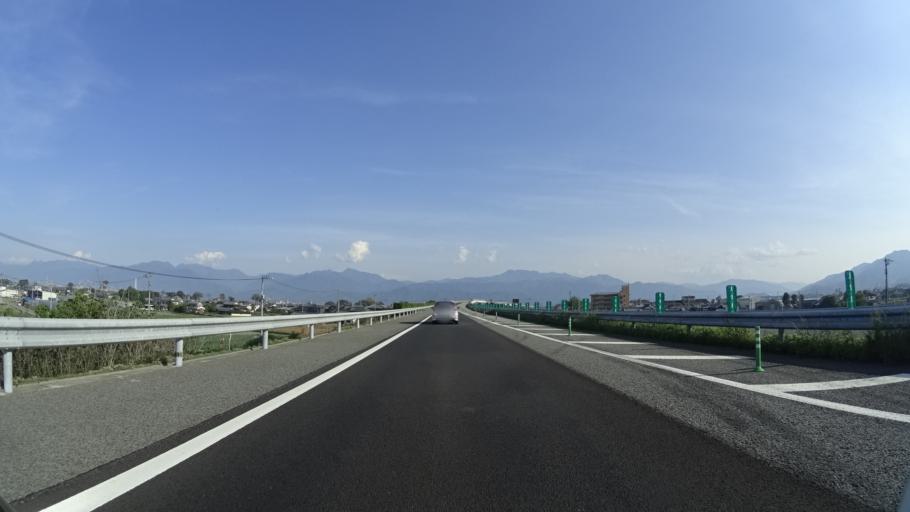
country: JP
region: Ehime
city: Saijo
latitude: 33.9552
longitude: 133.0678
